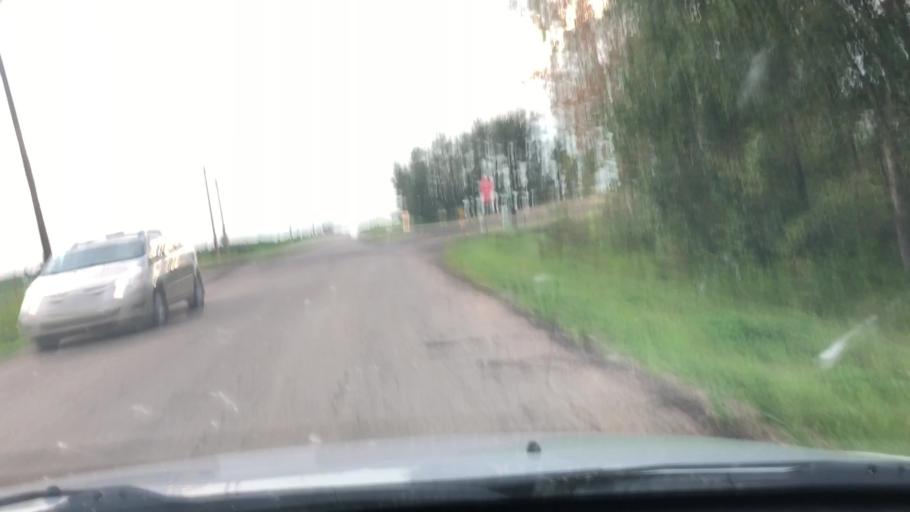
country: CA
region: Alberta
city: Devon
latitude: 53.4250
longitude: -113.6886
